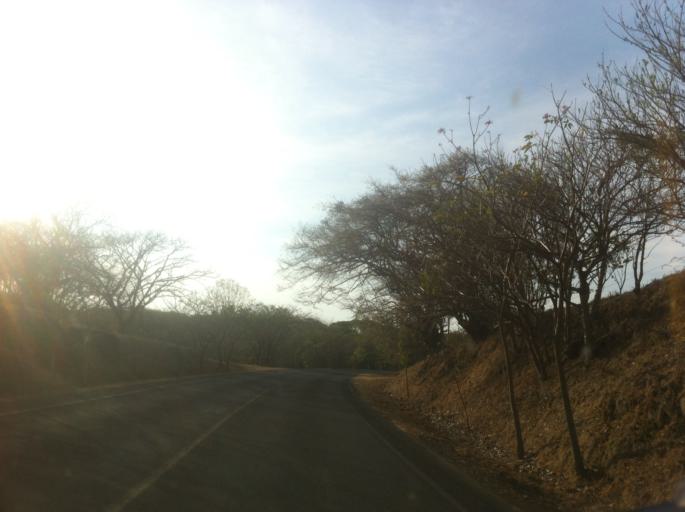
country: NI
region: Rivas
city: Cardenas
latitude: 11.2823
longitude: -85.6726
